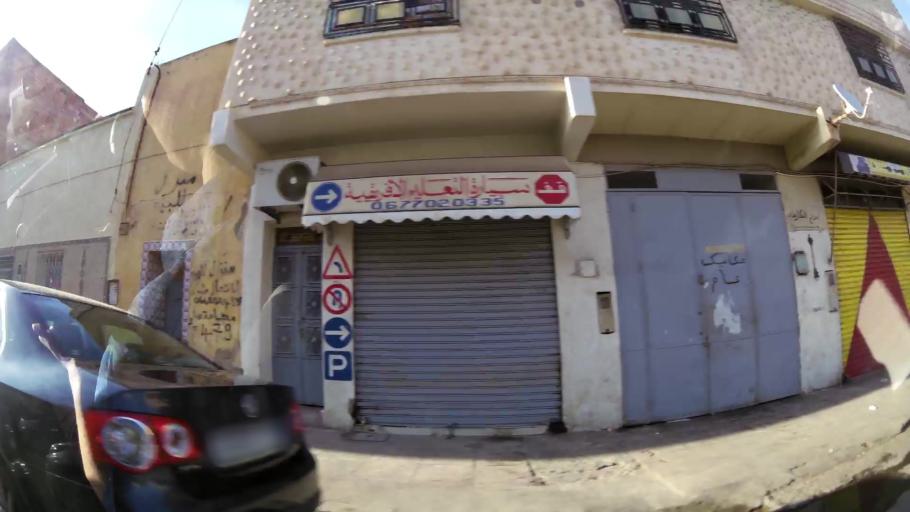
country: MA
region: Oriental
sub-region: Oujda-Angad
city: Oujda
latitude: 34.6768
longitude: -1.9112
